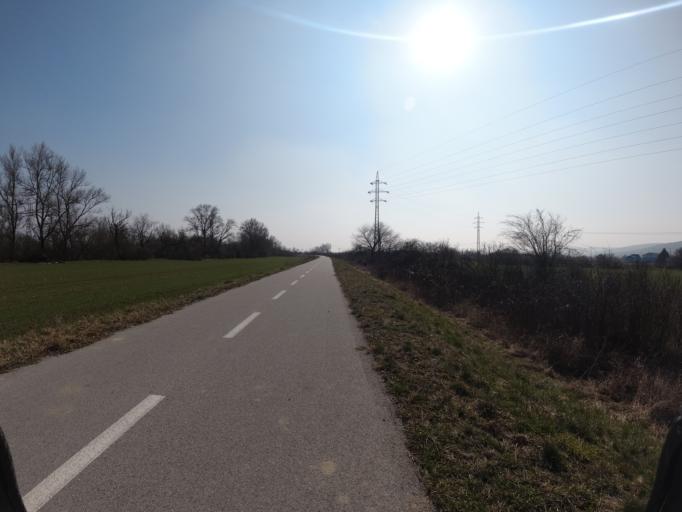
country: SK
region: Trenciansky
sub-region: Okres Nove Mesto nad Vahom
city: Nove Mesto nad Vahom
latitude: 48.7423
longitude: 17.8475
